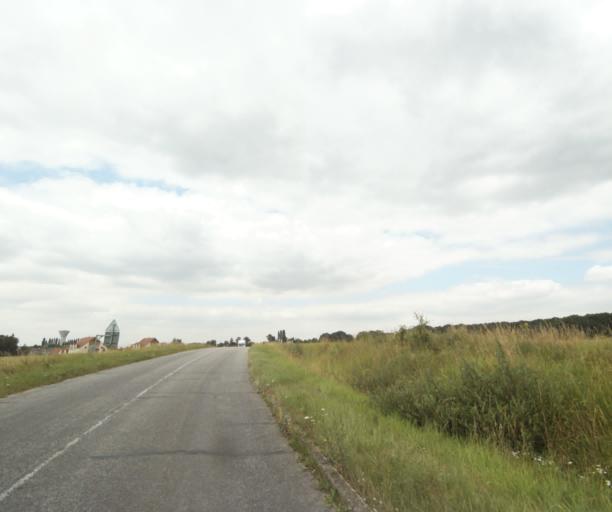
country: FR
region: Centre
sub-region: Departement du Loiret
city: Chanteau
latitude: 47.9647
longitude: 1.9781
